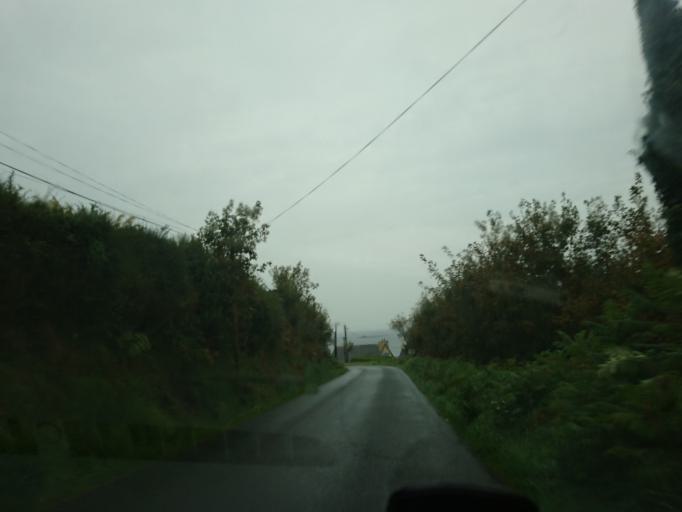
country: FR
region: Brittany
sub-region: Departement du Finistere
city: Plouguerneau
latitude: 48.6256
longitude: -4.4588
